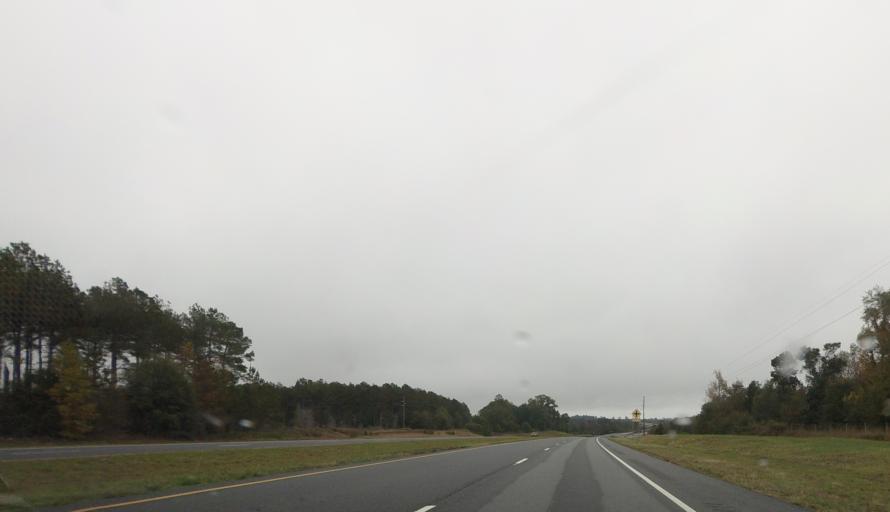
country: US
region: Georgia
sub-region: Taylor County
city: Reynolds
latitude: 32.5457
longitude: -84.0058
